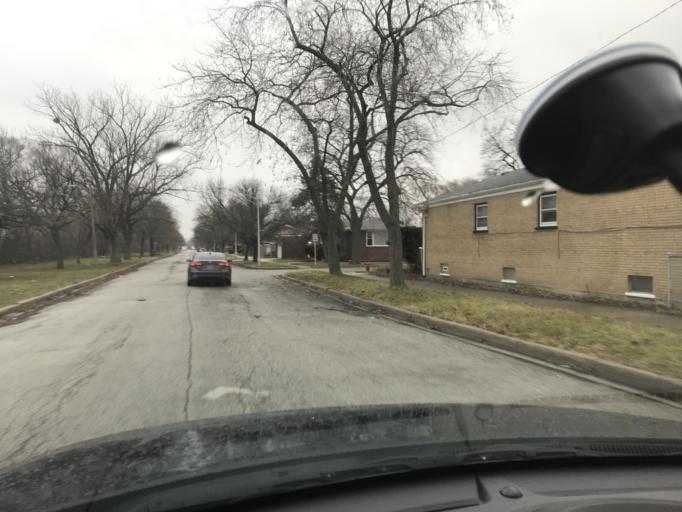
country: US
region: Illinois
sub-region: Cook County
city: Calumet Park
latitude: 41.7211
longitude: -87.6339
